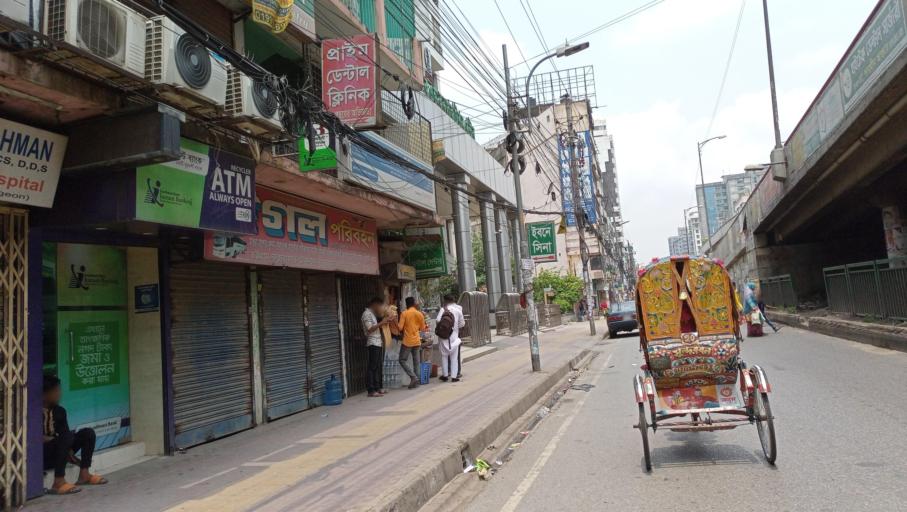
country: BD
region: Dhaka
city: Paltan
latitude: 23.7508
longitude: 90.4132
